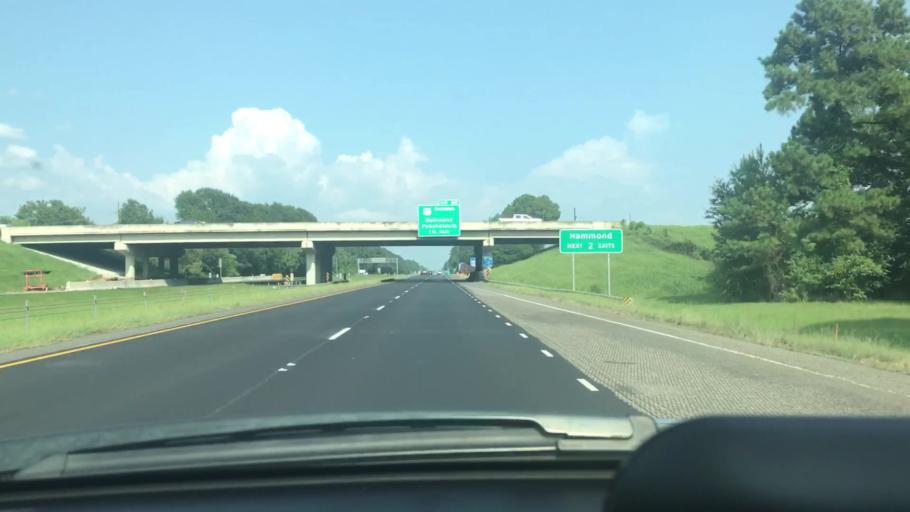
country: US
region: Louisiana
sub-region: Tangipahoa Parish
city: Hammond
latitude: 30.4789
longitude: -90.4838
